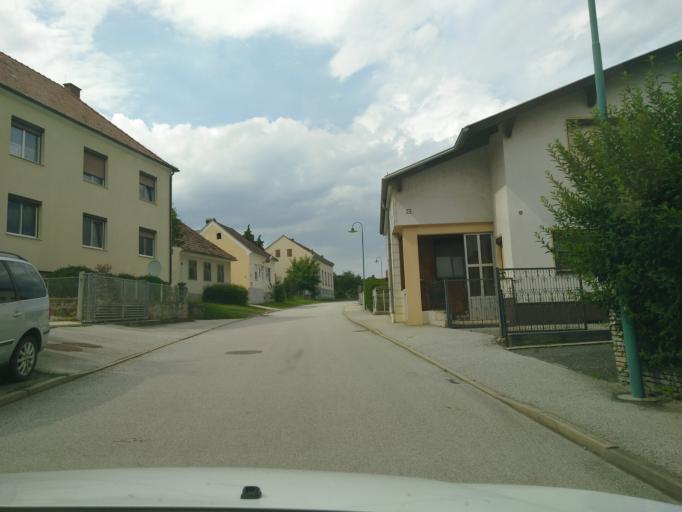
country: AT
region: Burgenland
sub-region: Politischer Bezirk Oberwart
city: Oberschutzen
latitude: 47.3488
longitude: 16.2056
